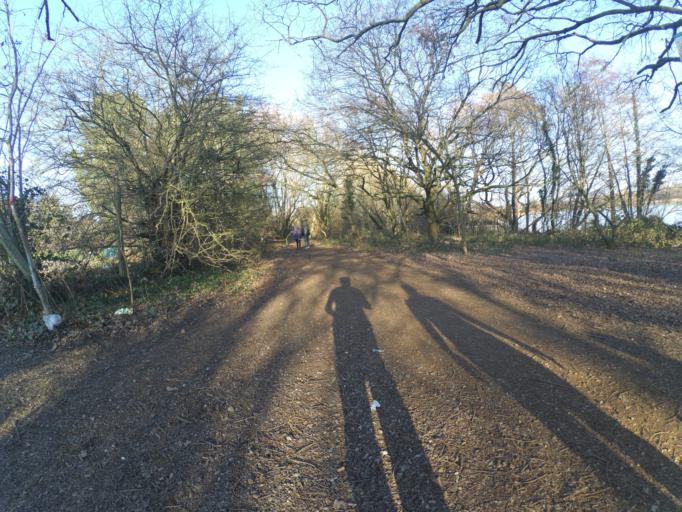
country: GB
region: England
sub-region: Greater London
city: Hendon
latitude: 51.5726
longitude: -0.2463
